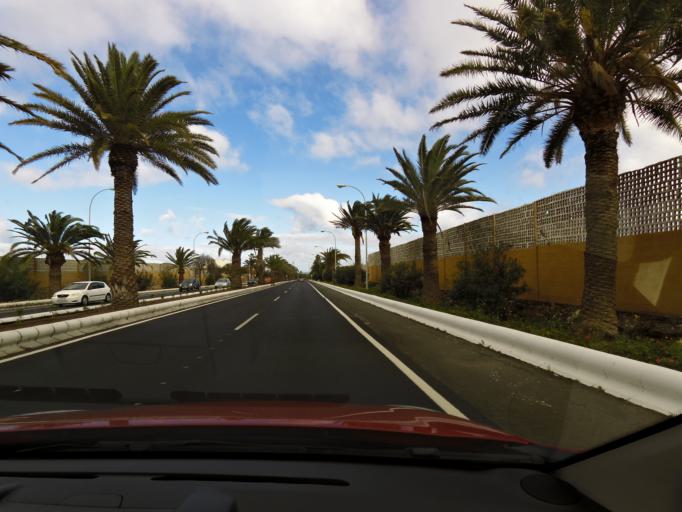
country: ES
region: Canary Islands
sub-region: Provincia de Las Palmas
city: Telde
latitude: 28.0044
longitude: -15.3973
